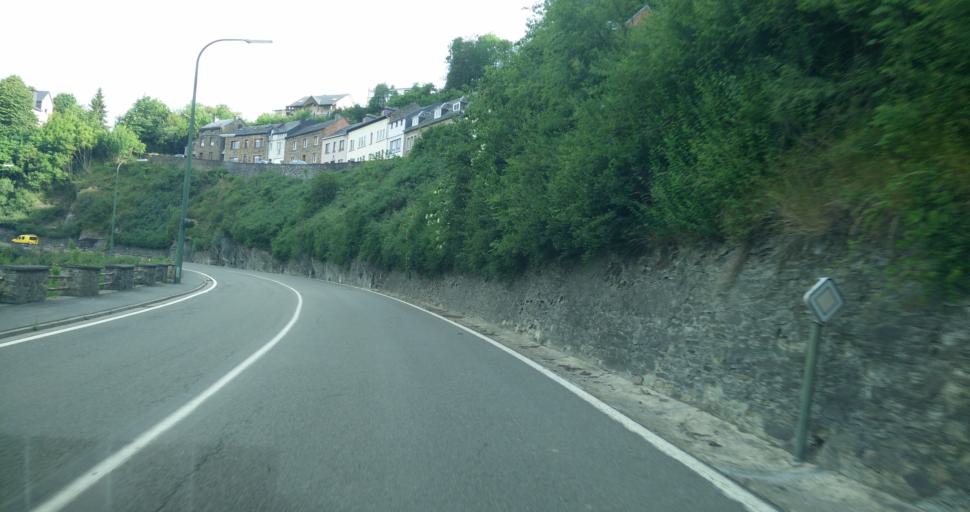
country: BE
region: Wallonia
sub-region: Province du Luxembourg
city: Houffalize
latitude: 50.1345
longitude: 5.7902
